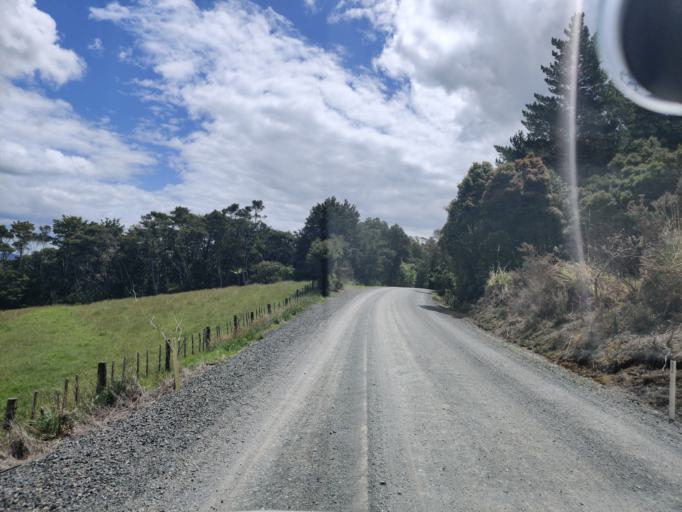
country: NZ
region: Northland
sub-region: Far North District
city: Paihia
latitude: -35.2595
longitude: 174.0620
